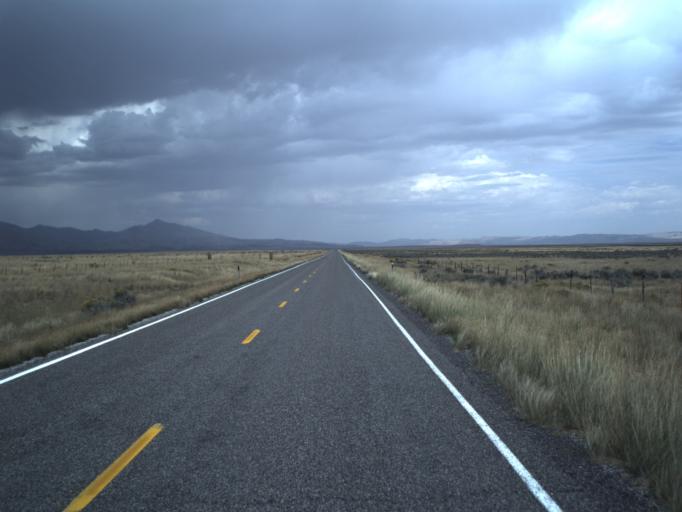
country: US
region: Idaho
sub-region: Oneida County
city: Malad City
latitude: 41.8898
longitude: -113.1124
